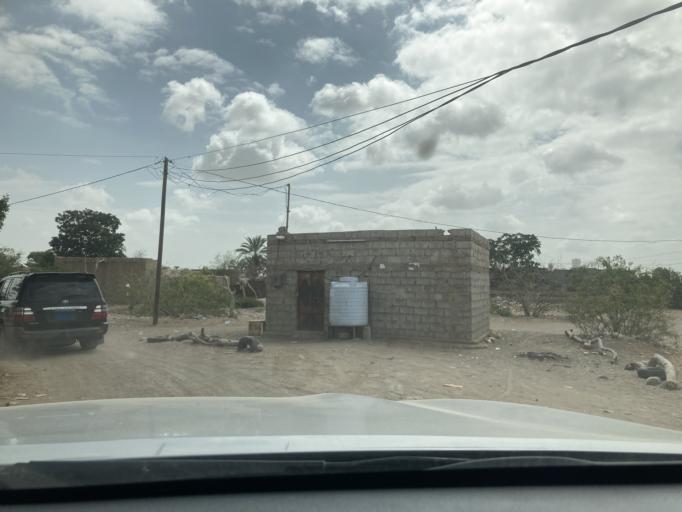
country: YE
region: Lahij
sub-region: Al  Hawtah
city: Lahij
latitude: 13.0169
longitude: 45.0037
